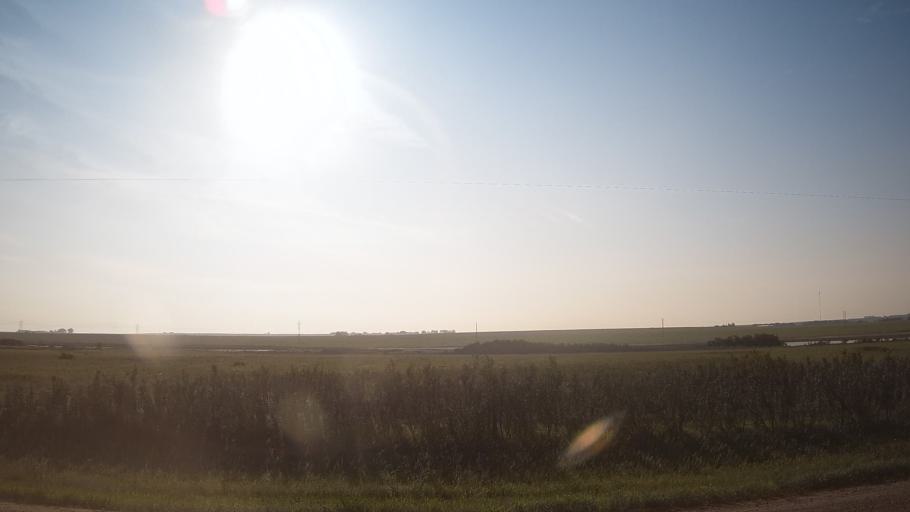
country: CA
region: Saskatchewan
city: Saskatoon
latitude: 51.8229
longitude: -106.5239
